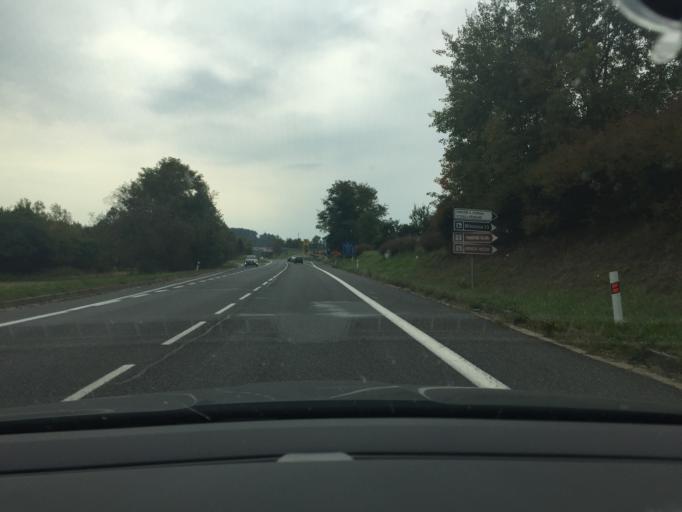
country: CZ
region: Central Bohemia
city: Milin
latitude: 49.6421
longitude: 14.0503
